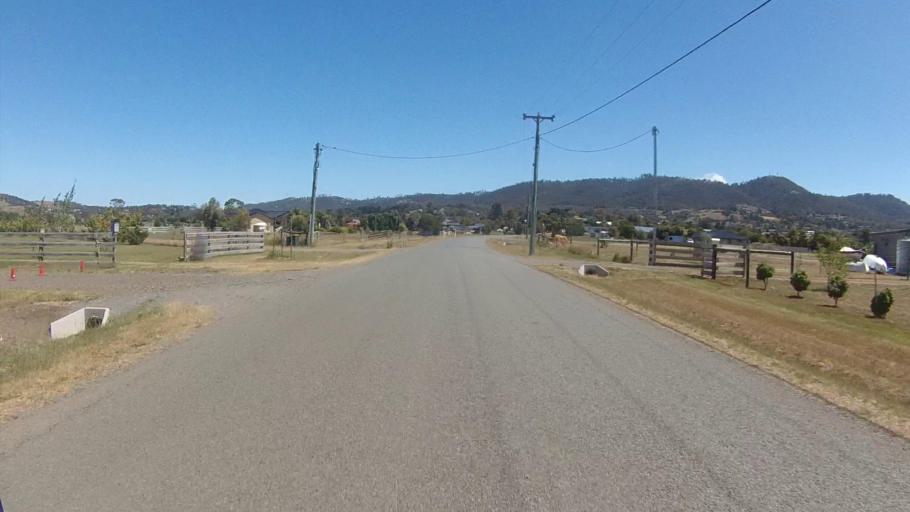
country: AU
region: Tasmania
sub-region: Clarence
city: Seven Mile Beach
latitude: -42.8520
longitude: 147.4910
